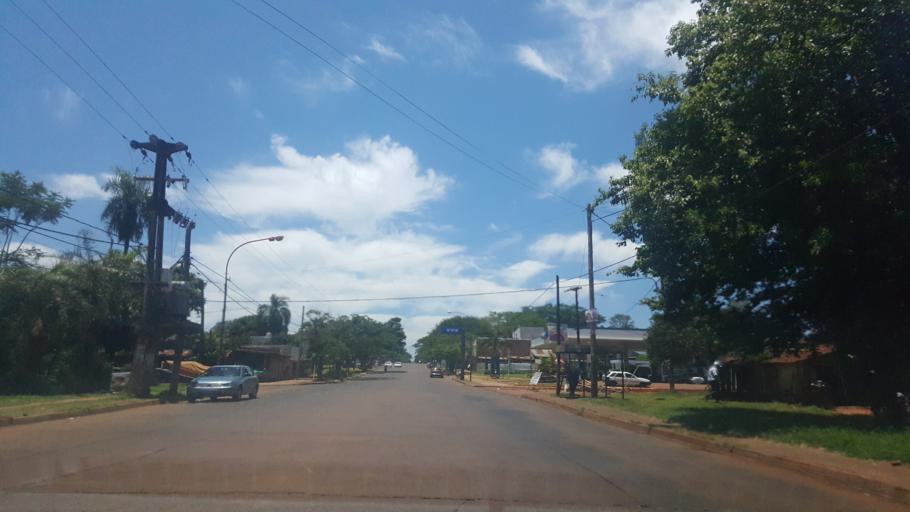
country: AR
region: Misiones
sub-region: Departamento de Capital
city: Posadas
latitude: -27.3668
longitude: -55.9361
